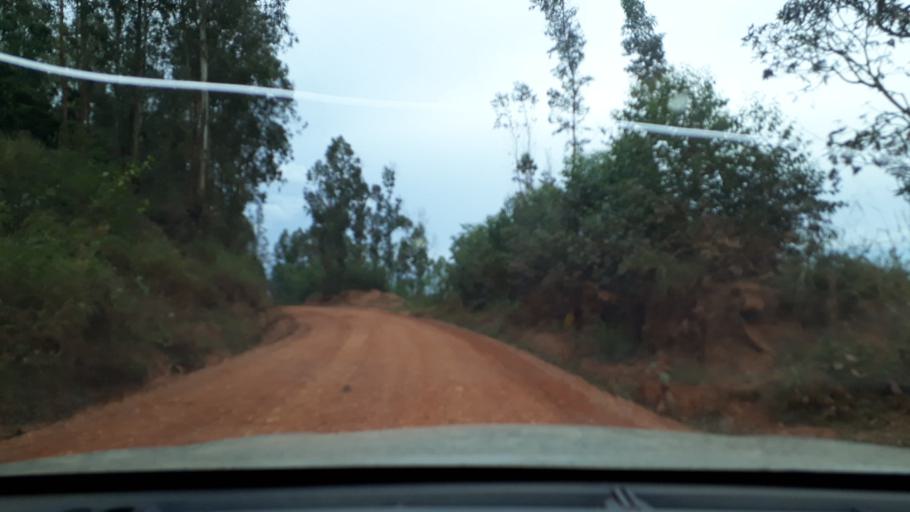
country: CD
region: Eastern Province
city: Bunia
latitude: 1.7812
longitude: 30.3893
